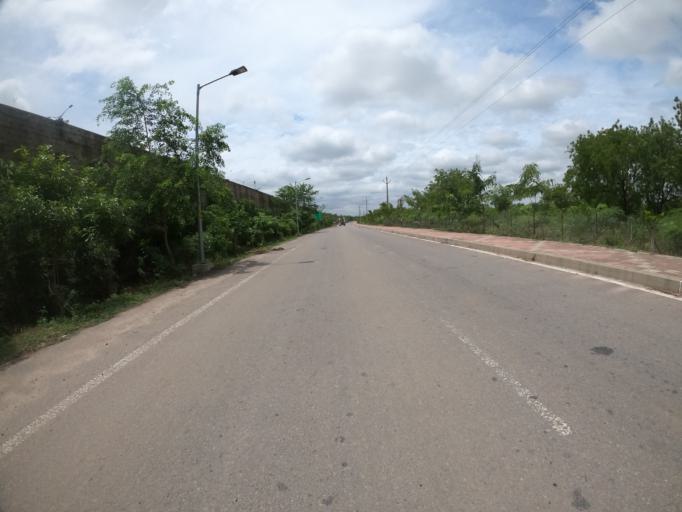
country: IN
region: Telangana
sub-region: Rangareddi
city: Balapur
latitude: 17.2836
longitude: 78.3825
